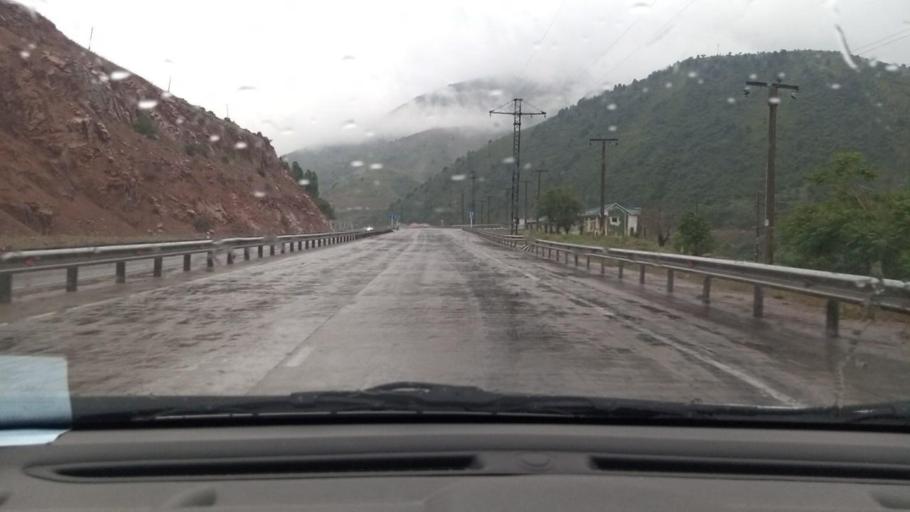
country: UZ
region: Toshkent
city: Angren
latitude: 41.1511
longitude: 70.4281
